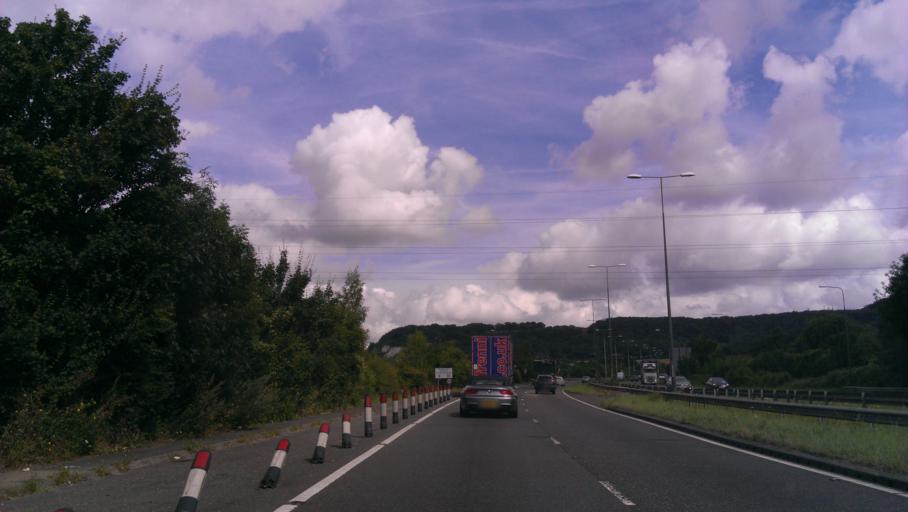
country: GB
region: England
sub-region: Kent
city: Boxley
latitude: 51.3057
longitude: 0.5120
